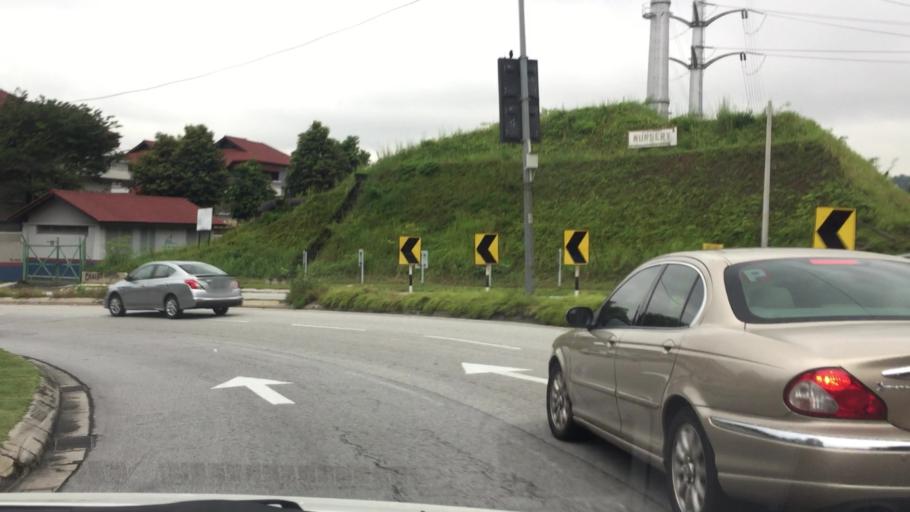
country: MY
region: Kuala Lumpur
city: Kuala Lumpur
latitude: 3.1707
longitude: 101.6636
